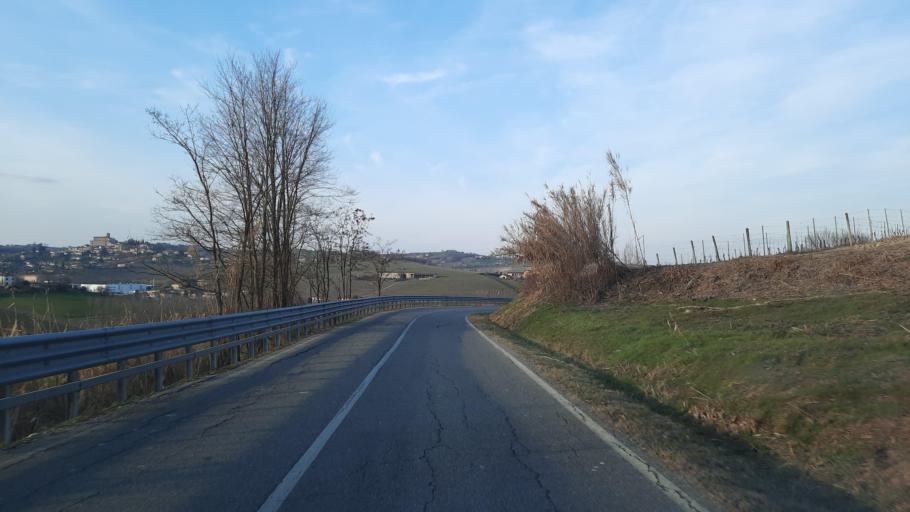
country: IT
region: Piedmont
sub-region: Provincia di Alessandria
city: Terruggia
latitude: 45.0938
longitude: 8.4313
